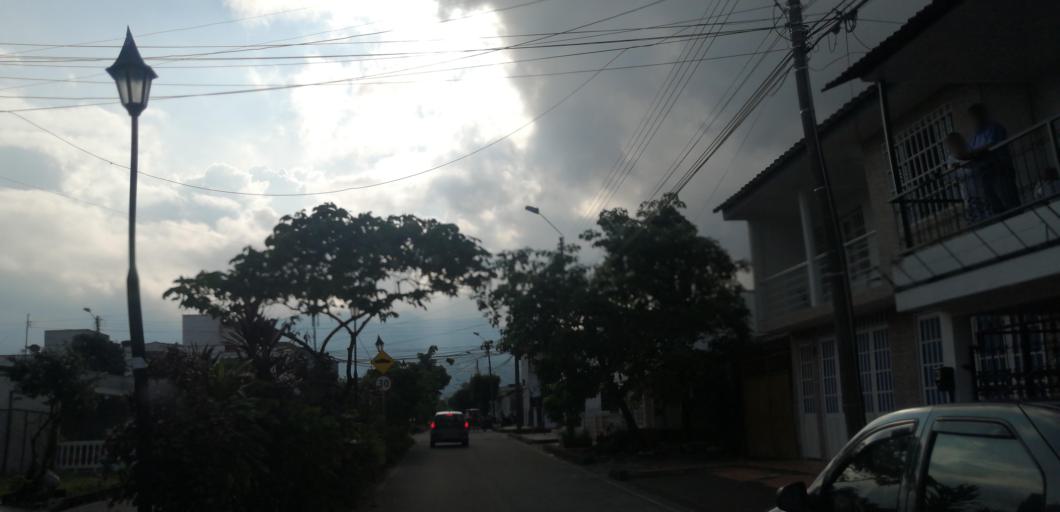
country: CO
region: Meta
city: Acacias
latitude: 3.9861
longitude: -73.7730
